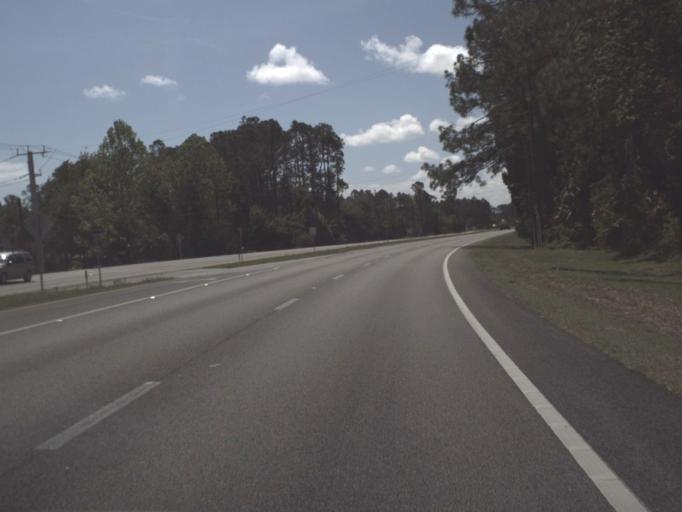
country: US
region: Florida
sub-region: Flagler County
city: Bunnell
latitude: 29.4057
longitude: -81.1962
